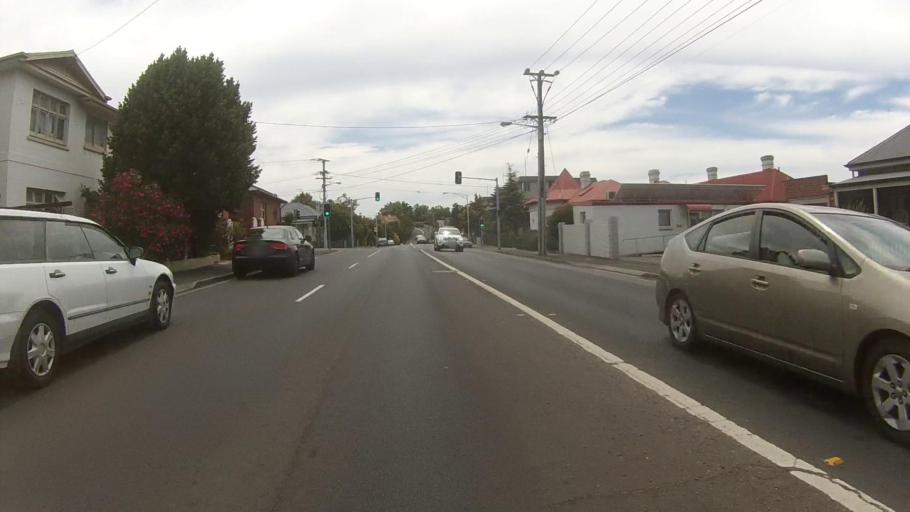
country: AU
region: Tasmania
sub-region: Hobart
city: Sandy Bay
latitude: -42.8960
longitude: 147.3233
